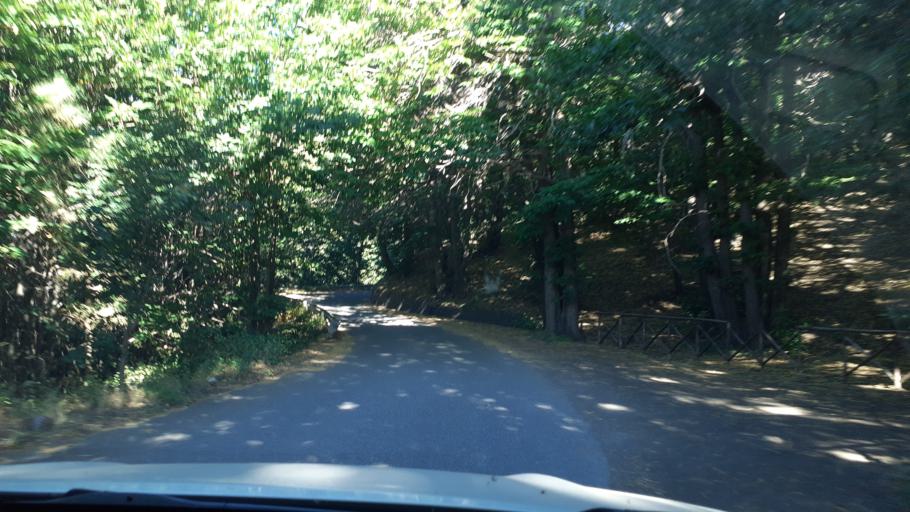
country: IT
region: Sicily
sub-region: Catania
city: Ragalna
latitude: 37.6879
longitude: 14.9854
